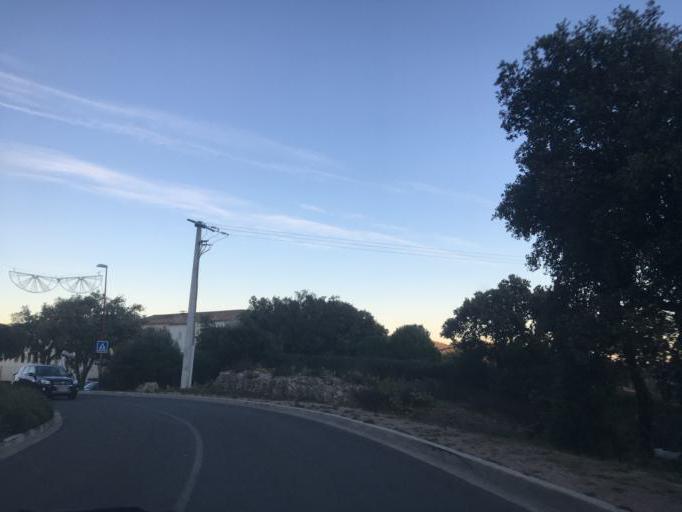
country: FR
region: Provence-Alpes-Cote d'Azur
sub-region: Departement du Var
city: Le Plan-de-la-Tour
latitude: 43.3367
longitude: 6.5480
